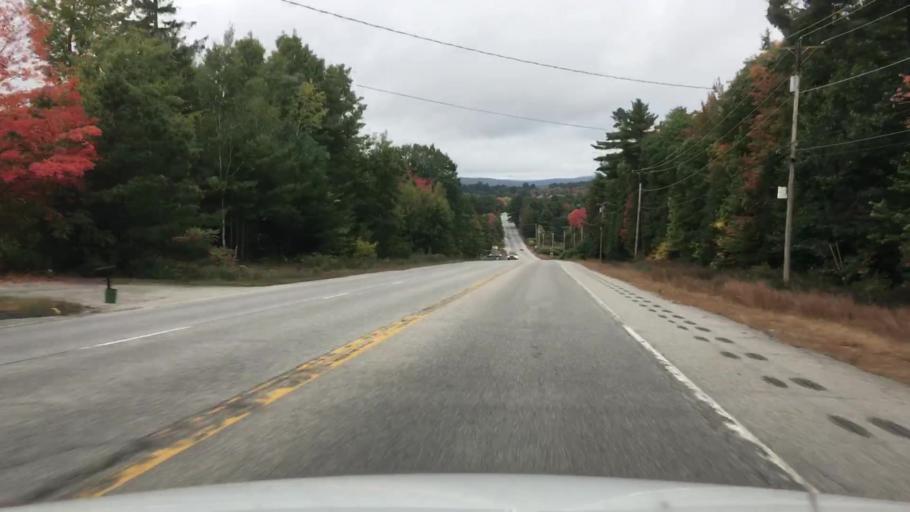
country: US
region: Maine
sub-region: Oxford County
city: Oxford
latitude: 44.1242
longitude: -70.4501
